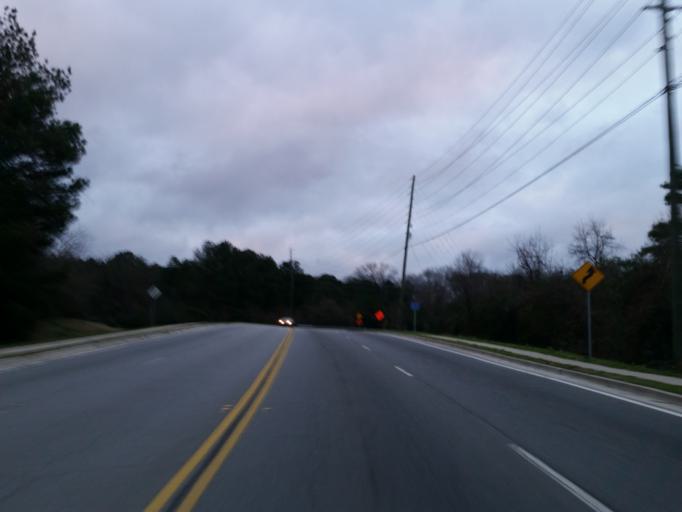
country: US
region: Georgia
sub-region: Cobb County
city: Fair Oaks
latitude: 33.9016
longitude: -84.5795
